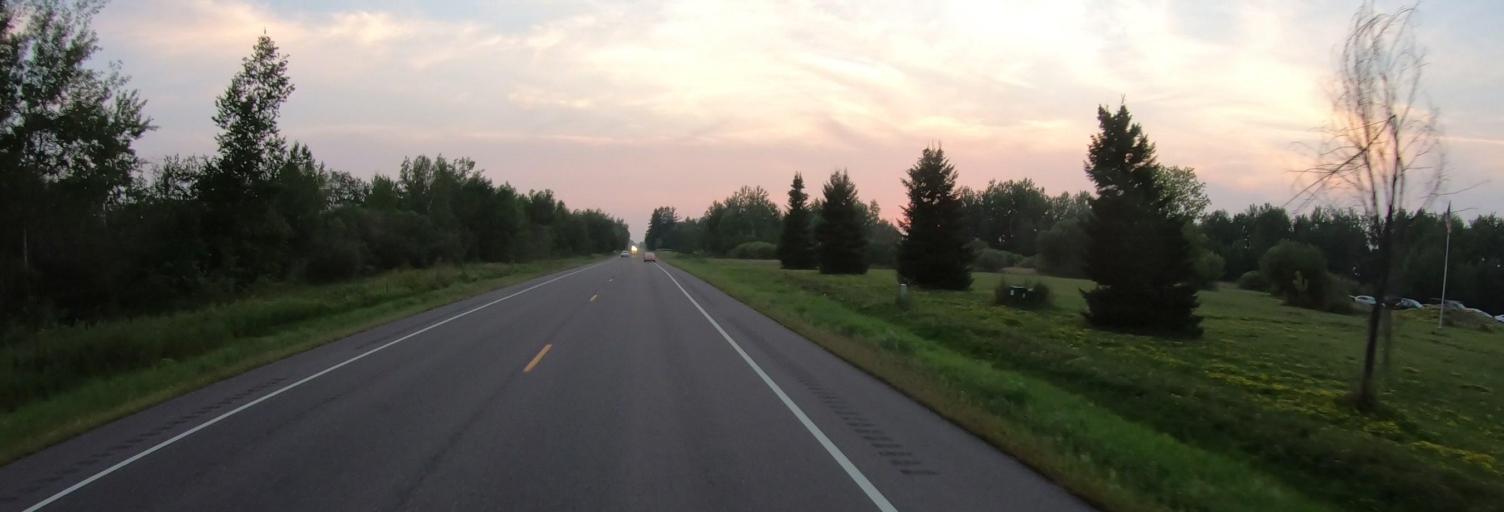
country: US
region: Minnesota
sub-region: Pine County
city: Rock Creek
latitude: 45.7735
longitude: -92.8755
